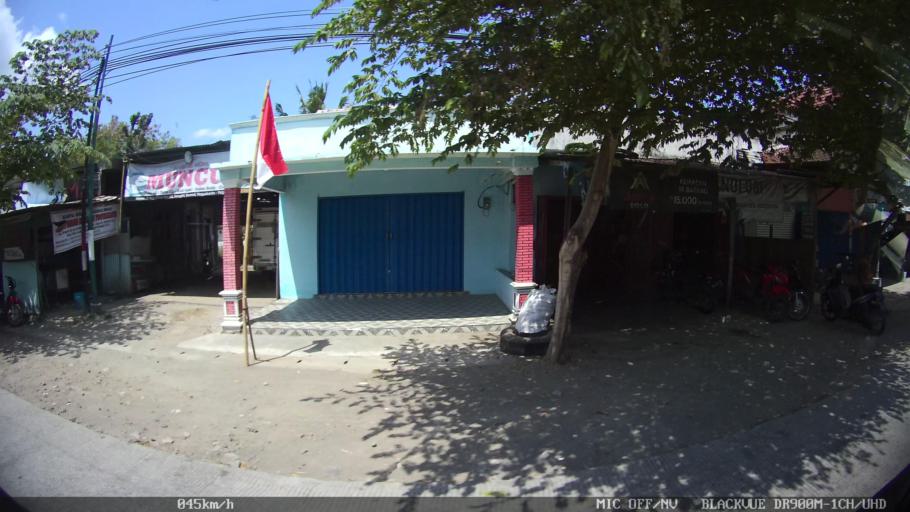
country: ID
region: Daerah Istimewa Yogyakarta
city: Pundong
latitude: -7.9213
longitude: 110.3757
